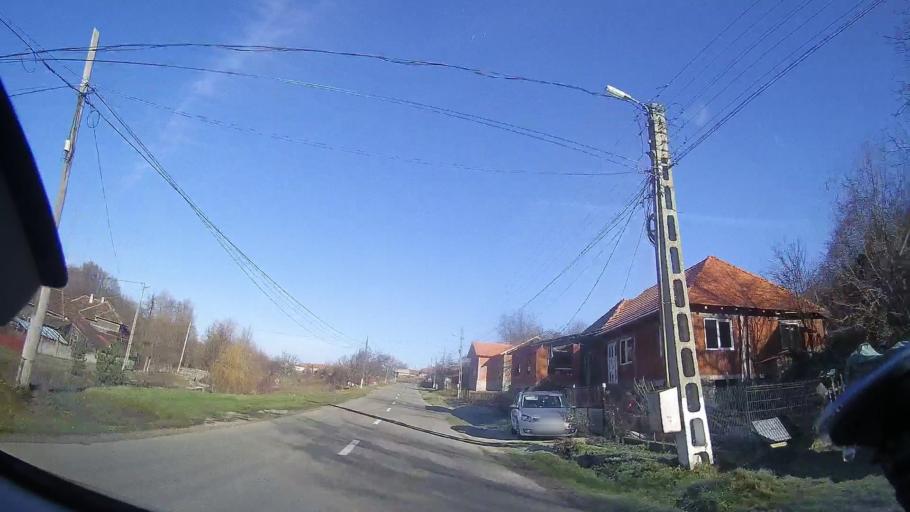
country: RO
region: Bihor
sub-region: Comuna Bratca
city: Bratca
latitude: 46.9317
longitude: 22.6018
